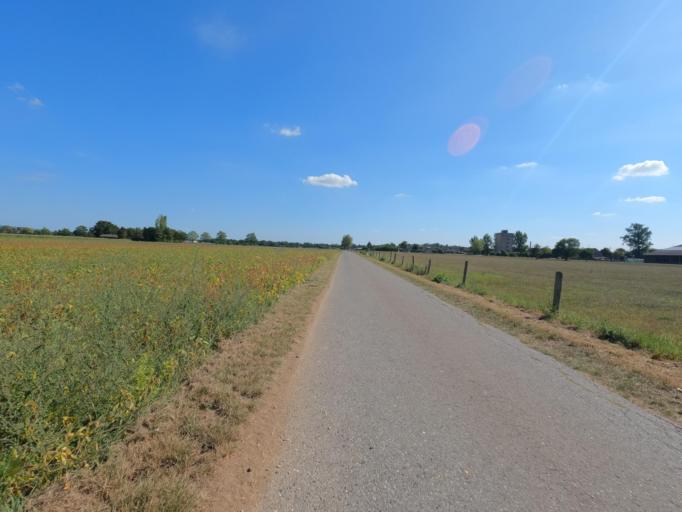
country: DE
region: North Rhine-Westphalia
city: Julich
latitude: 50.9341
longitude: 6.3266
